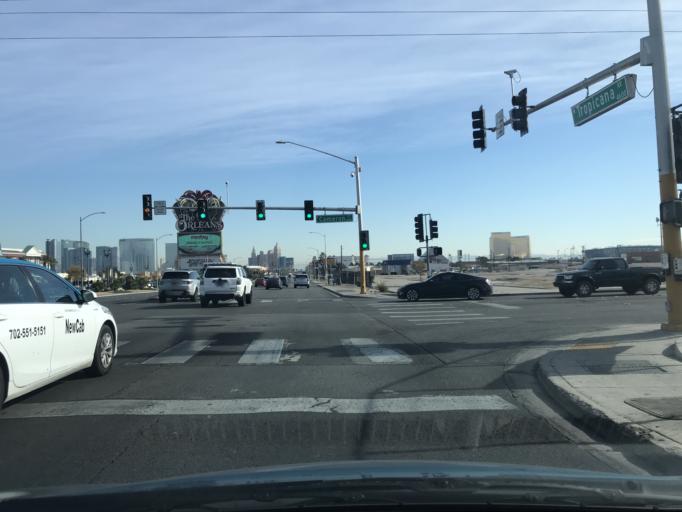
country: US
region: Nevada
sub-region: Clark County
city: Spring Valley
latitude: 36.1008
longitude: -115.2043
